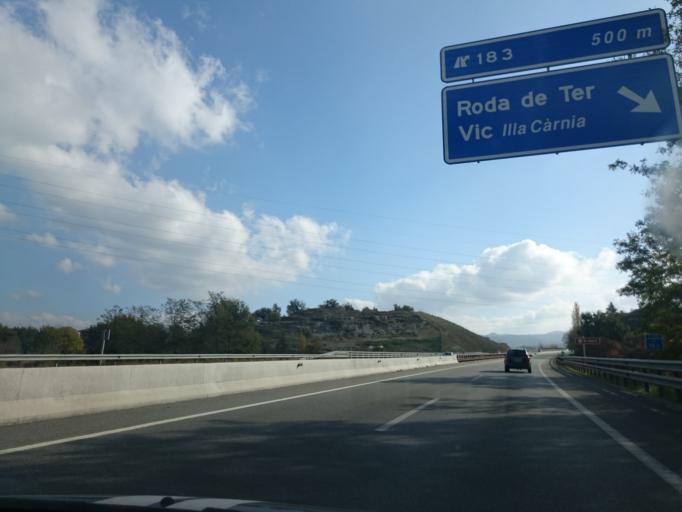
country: ES
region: Catalonia
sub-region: Provincia de Barcelona
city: Vic
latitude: 41.9601
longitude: 2.2785
